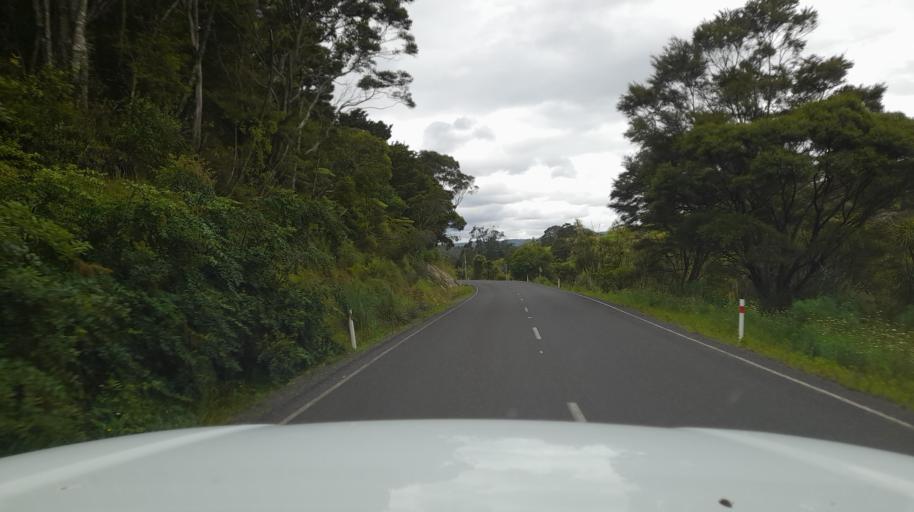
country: NZ
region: Northland
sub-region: Far North District
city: Taipa
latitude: -35.2427
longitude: 173.5348
